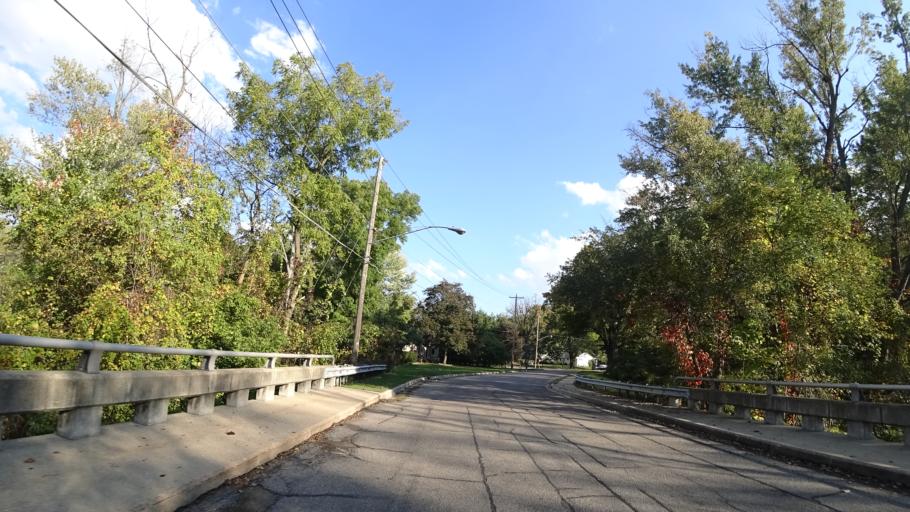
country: US
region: Michigan
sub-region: Saint Joseph County
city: Three Rivers
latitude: 41.9471
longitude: -85.6284
